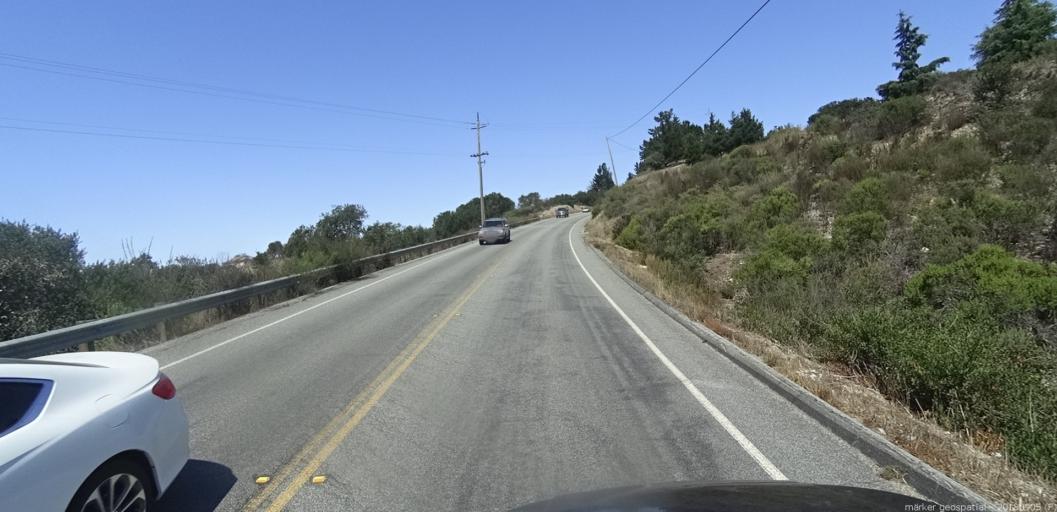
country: US
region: California
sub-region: Monterey County
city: Carmel Valley Village
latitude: 36.5385
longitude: -121.7530
